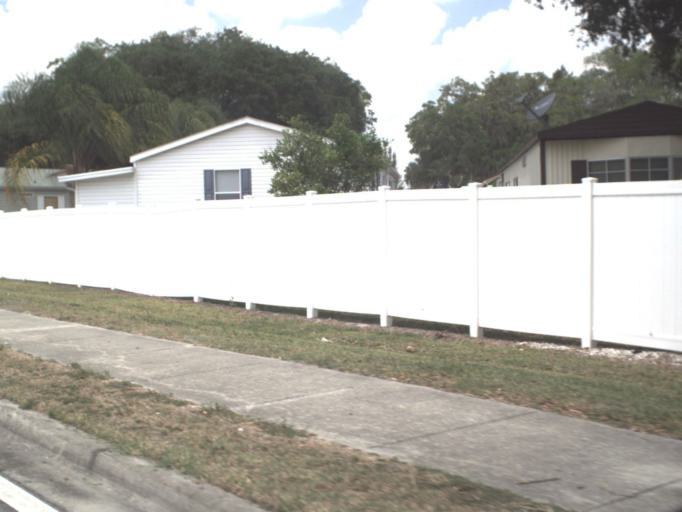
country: US
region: Florida
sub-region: Sumter County
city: Wildwood
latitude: 28.8471
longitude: -82.0405
